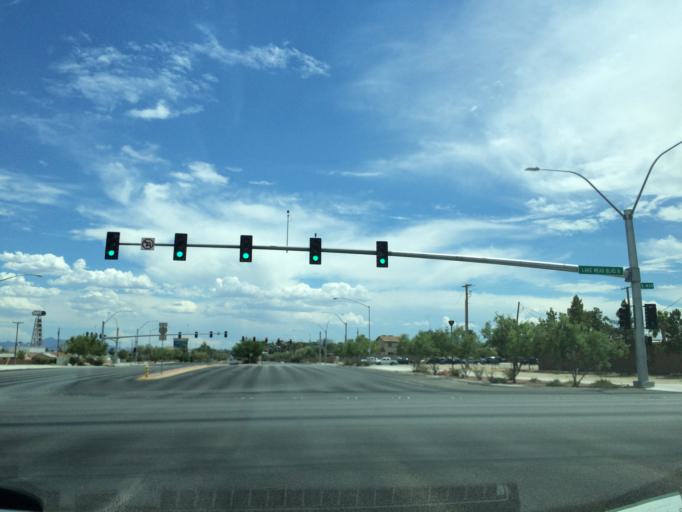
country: US
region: Nevada
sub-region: Clark County
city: North Las Vegas
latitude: 36.1972
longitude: -115.1341
